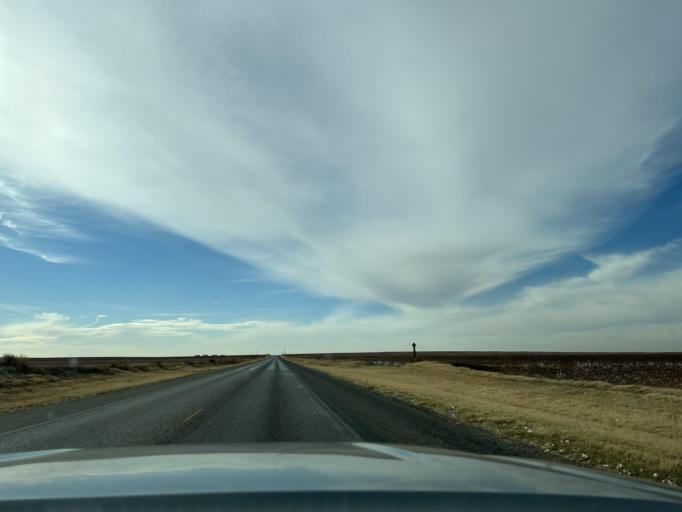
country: US
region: Texas
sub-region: Fisher County
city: Roby
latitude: 32.7418
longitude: -100.4470
